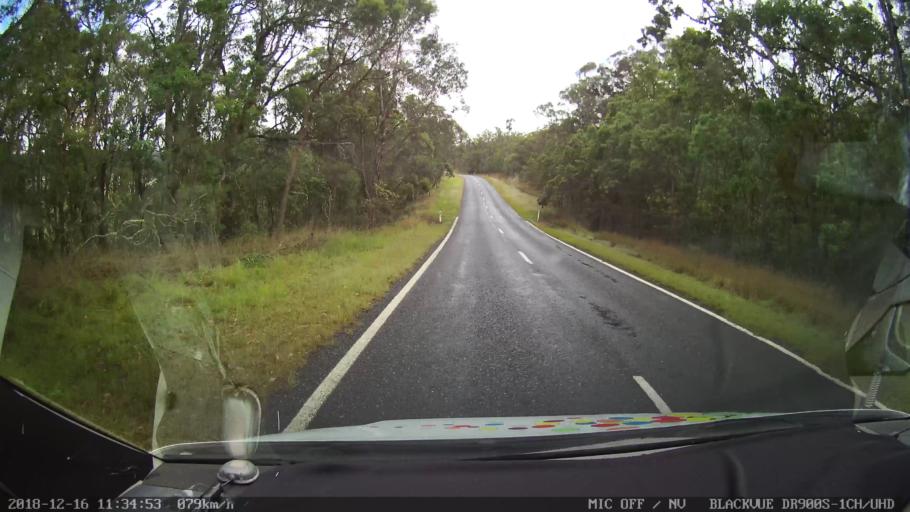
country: AU
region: New South Wales
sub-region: Tenterfield Municipality
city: Carrolls Creek
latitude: -28.9956
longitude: 152.1584
